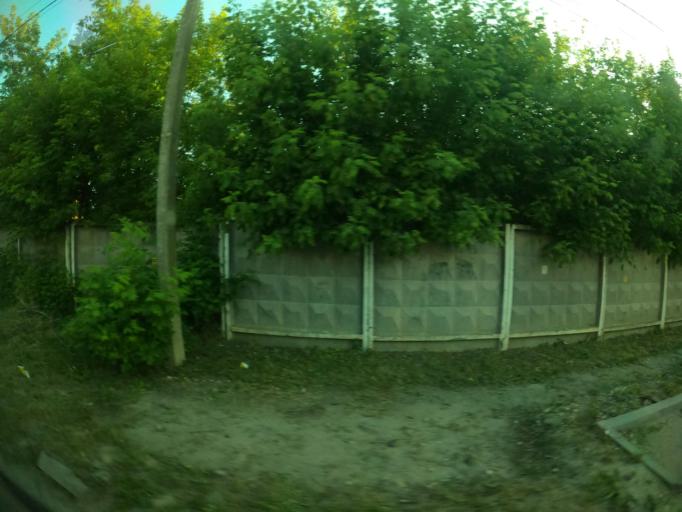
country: RU
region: Moskovskaya
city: Serpukhov
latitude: 54.9205
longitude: 37.4038
